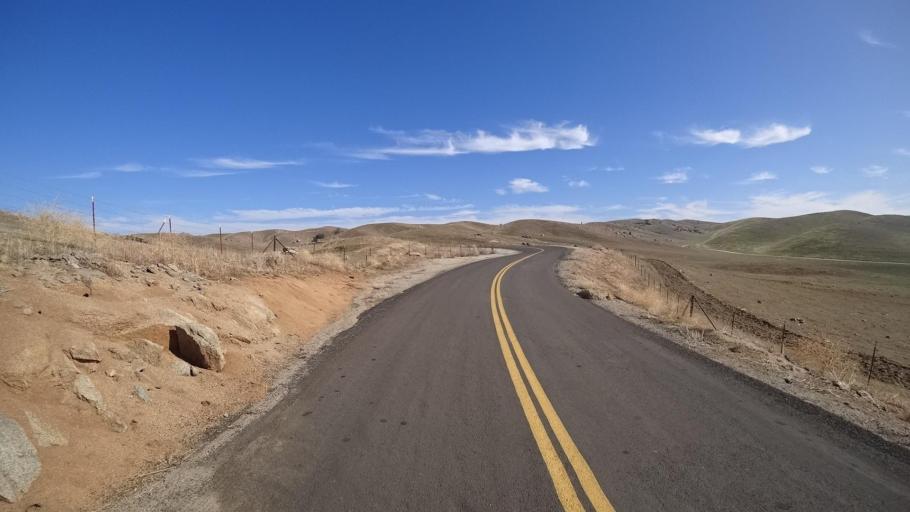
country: US
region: California
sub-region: Tulare County
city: Richgrove
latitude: 35.6824
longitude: -118.8931
